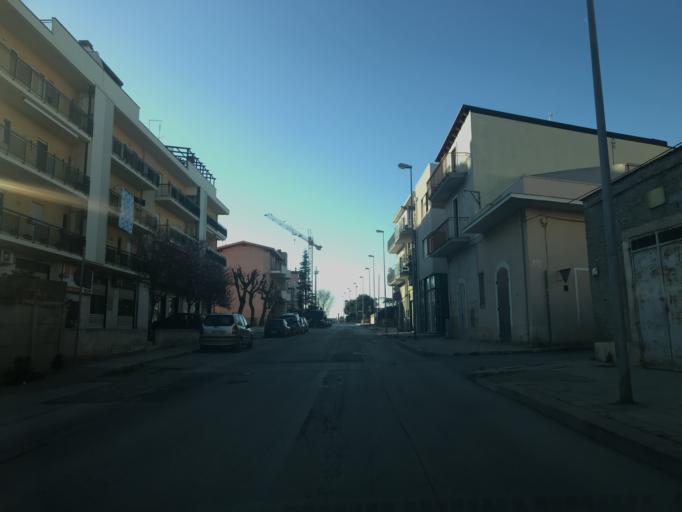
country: IT
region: Apulia
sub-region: Provincia di Bari
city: Corato
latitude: 41.1450
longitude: 16.4123
